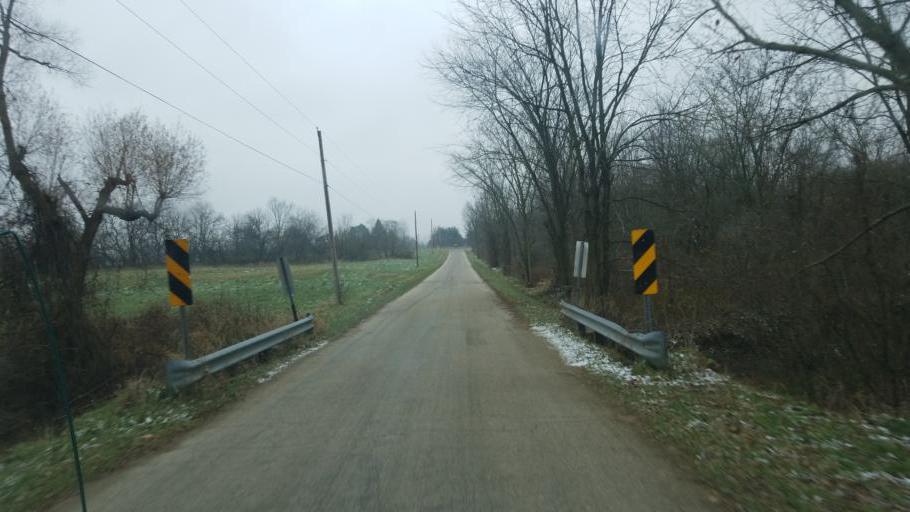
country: US
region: Ohio
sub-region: Huron County
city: New London
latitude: 41.0158
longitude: -82.3295
